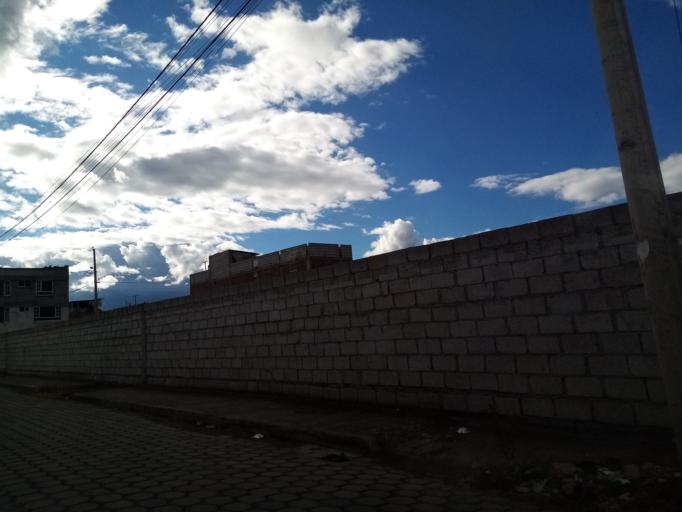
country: EC
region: Chimborazo
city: Riobamba
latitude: -1.6899
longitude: -78.6261
